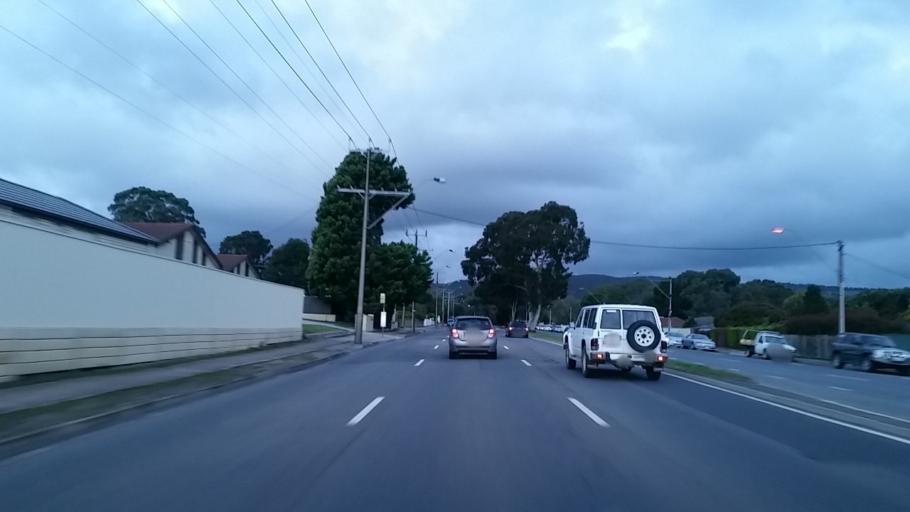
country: AU
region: South Australia
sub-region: Tea Tree Gully
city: Hope Valley
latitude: -34.8273
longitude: 138.7008
